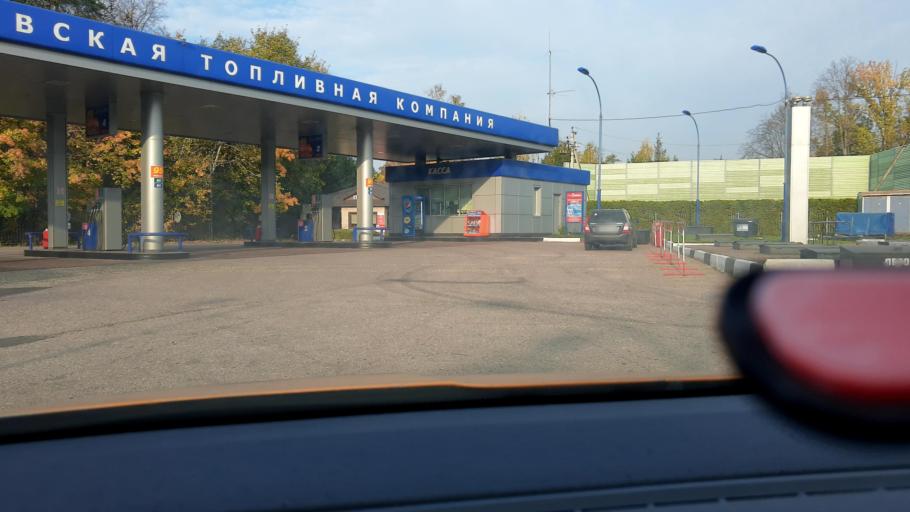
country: RU
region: Moskovskaya
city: Lesnoy Gorodok
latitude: 55.6466
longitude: 37.2454
